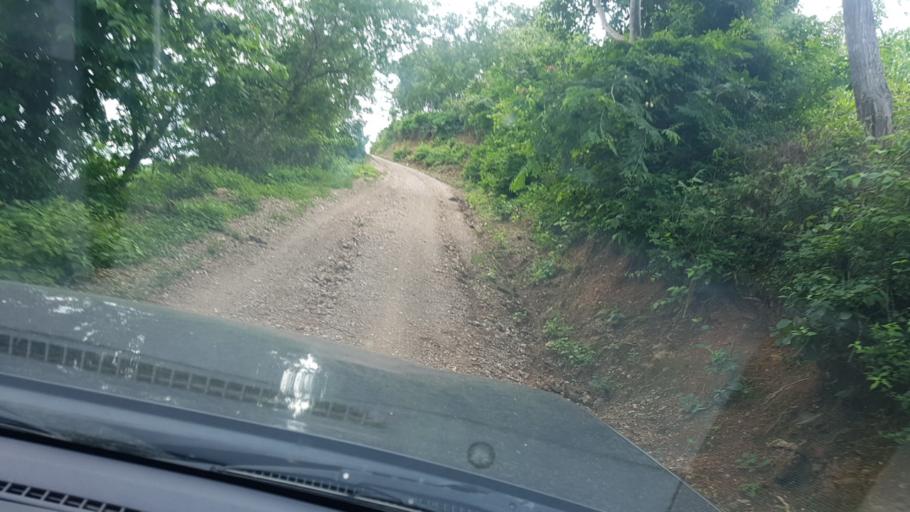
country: NI
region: Nueva Segovia
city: Ocotal
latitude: 13.5930
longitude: -86.4171
